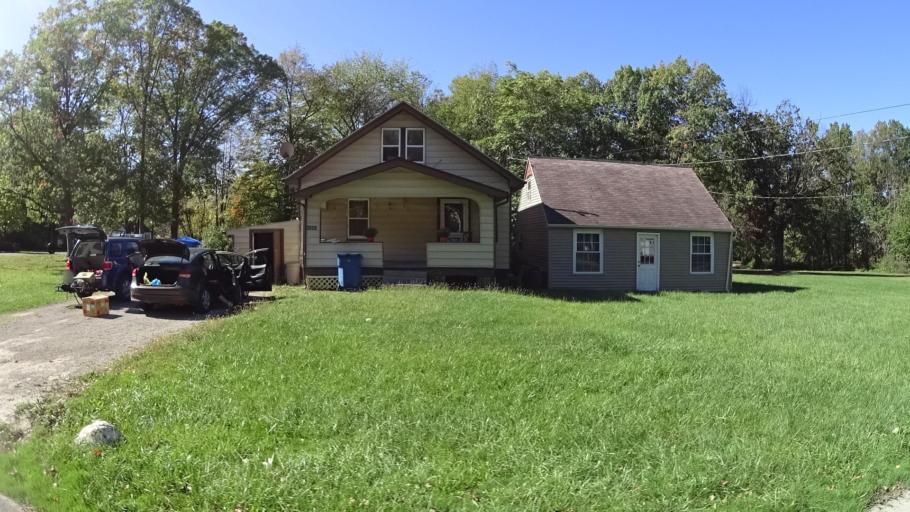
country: US
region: Ohio
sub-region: Lorain County
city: Lorain
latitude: 41.4361
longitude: -82.1667
